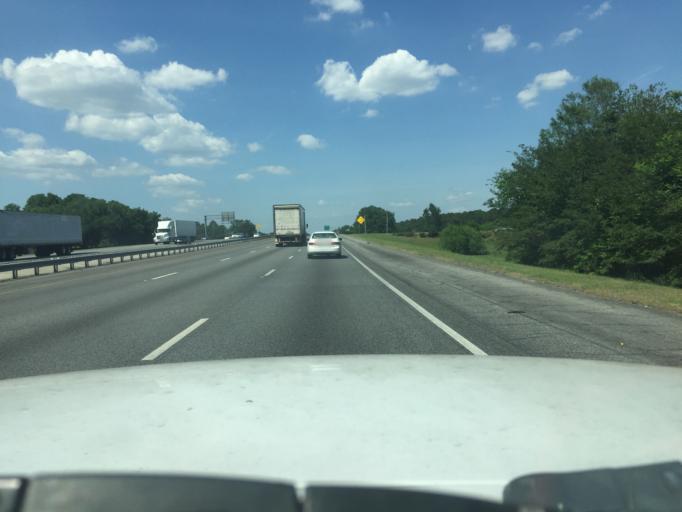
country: US
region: Georgia
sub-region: Chatham County
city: Pooler
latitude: 32.0714
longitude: -81.2472
